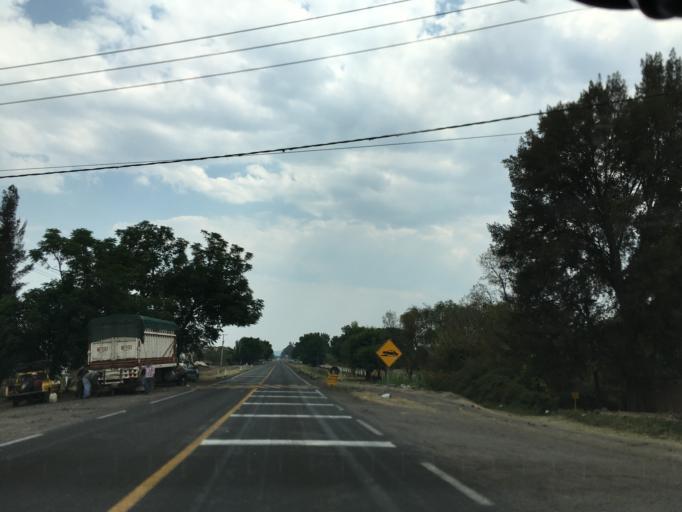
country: MX
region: Michoacan
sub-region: Cuitzeo
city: Cuamio
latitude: 20.0272
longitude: -101.1532
